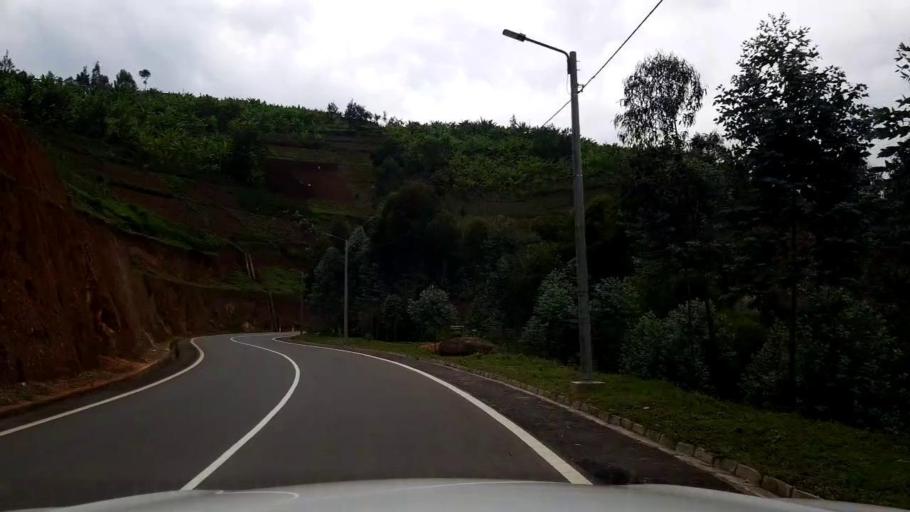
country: RW
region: Western Province
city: Kibuye
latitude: -1.9278
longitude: 29.3728
